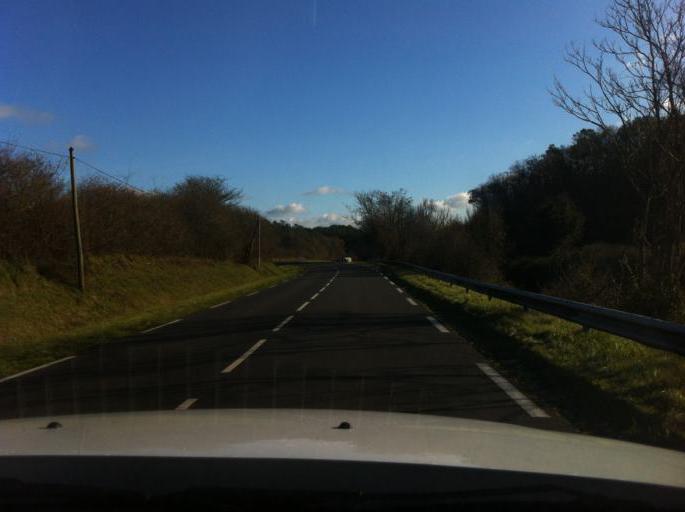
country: FR
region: Aquitaine
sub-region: Departement de la Dordogne
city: Rouffignac-Saint-Cernin-de-Reilhac
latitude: 45.0423
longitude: 0.8796
